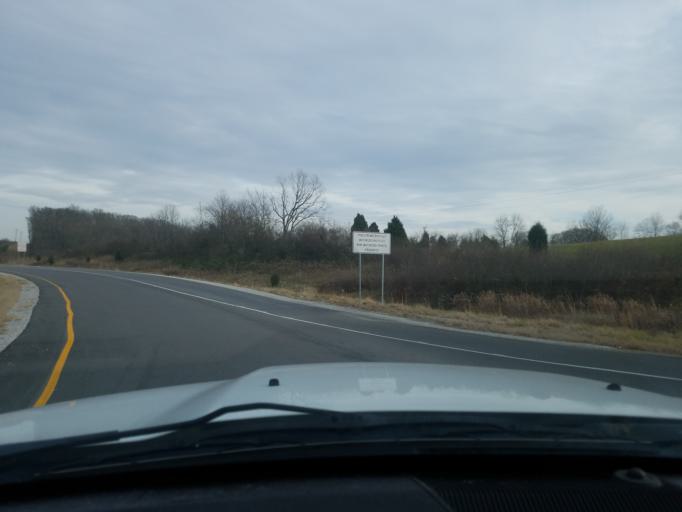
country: US
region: Indiana
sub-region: Dubois County
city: Ferdinand
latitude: 38.2048
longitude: -86.8658
